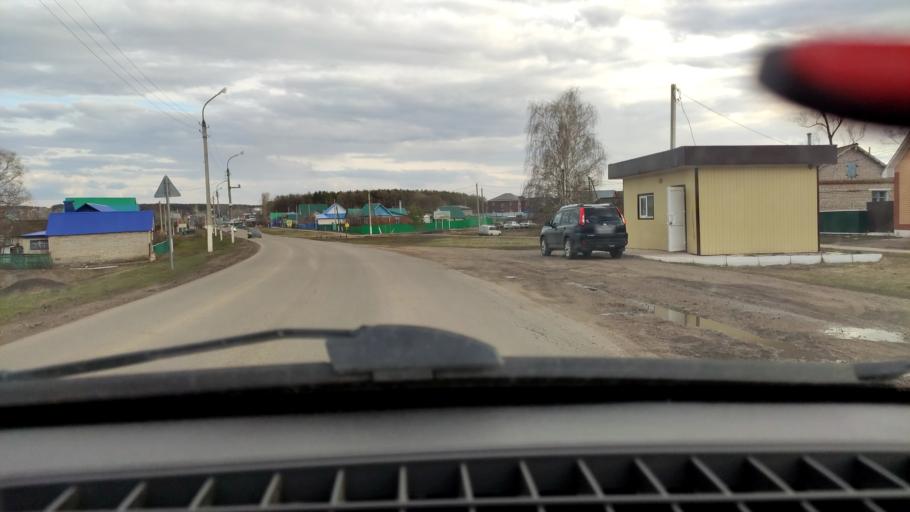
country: RU
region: Bashkortostan
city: Tolbazy
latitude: 54.0297
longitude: 55.8837
